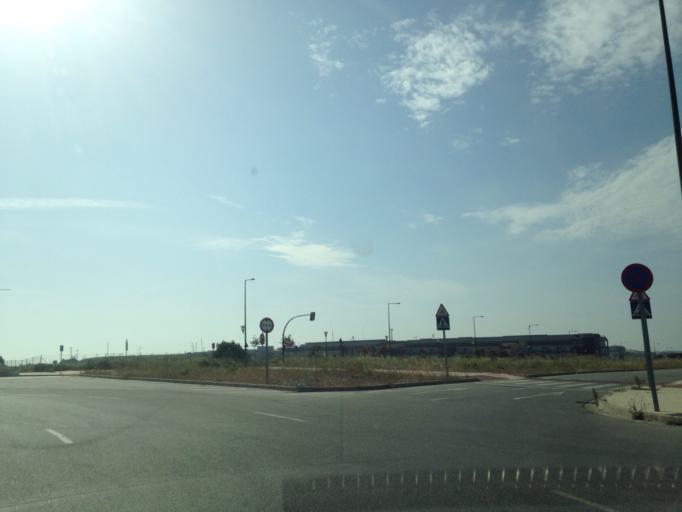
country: ES
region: Andalusia
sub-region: Provincia de Malaga
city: Malaga
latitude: 36.7187
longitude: -4.4955
